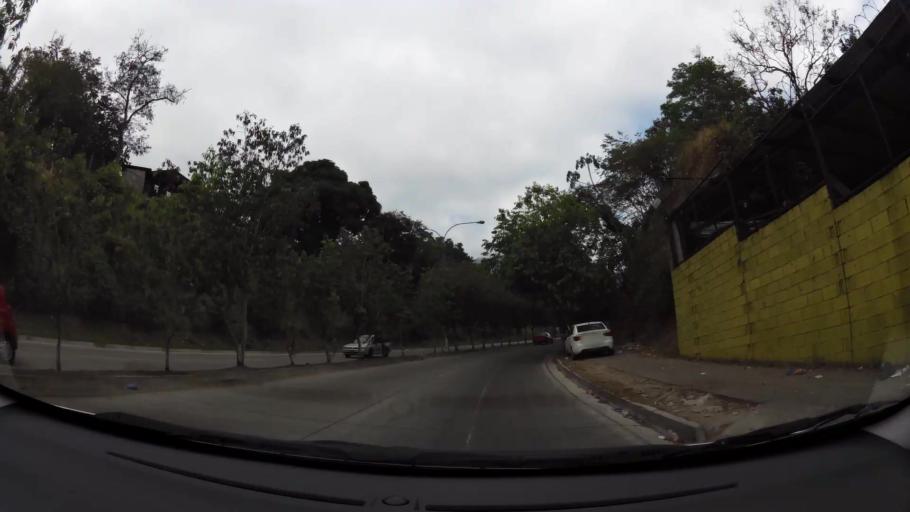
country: SV
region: San Salvador
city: Mejicanos
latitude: 13.7179
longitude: -89.2314
